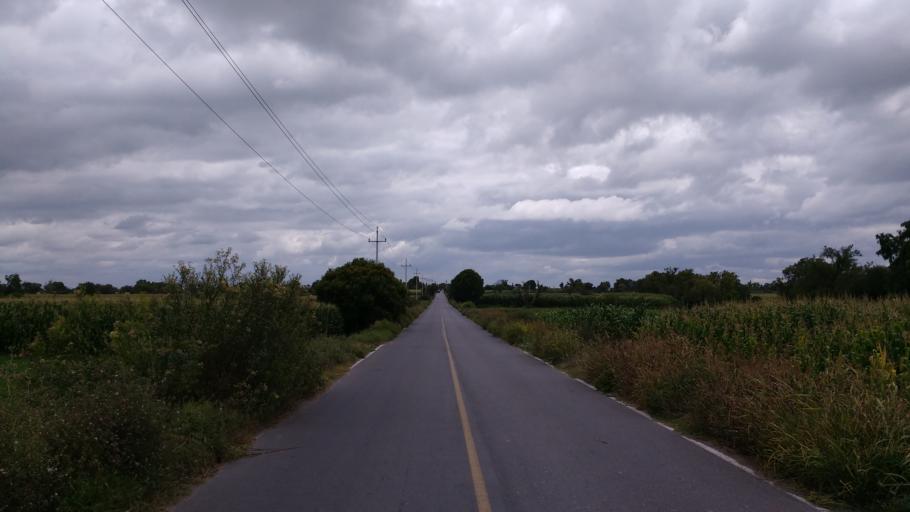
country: MX
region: Hidalgo
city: Mixquiahuala de Juarez
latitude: 20.2395
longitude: -99.2460
